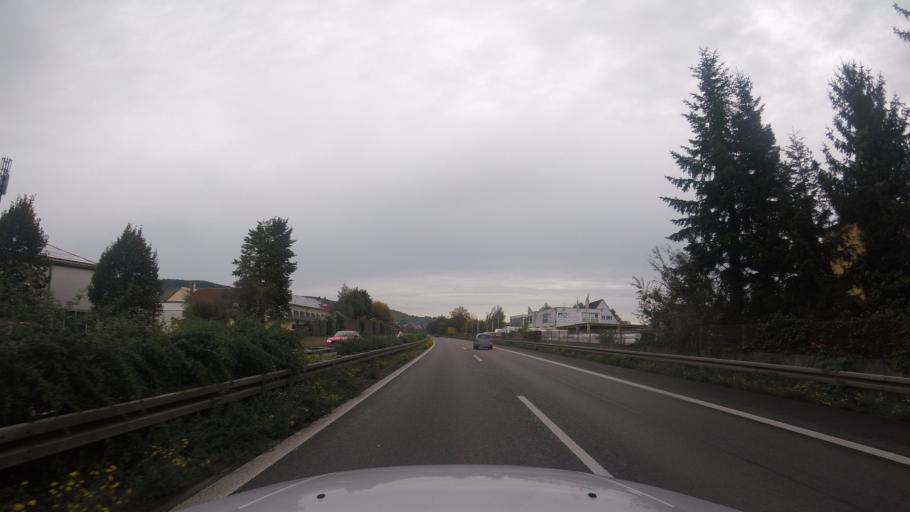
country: DE
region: Baden-Wuerttemberg
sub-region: Regierungsbezirk Stuttgart
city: Weinstadt-Endersbach
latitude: 48.8131
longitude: 9.4164
